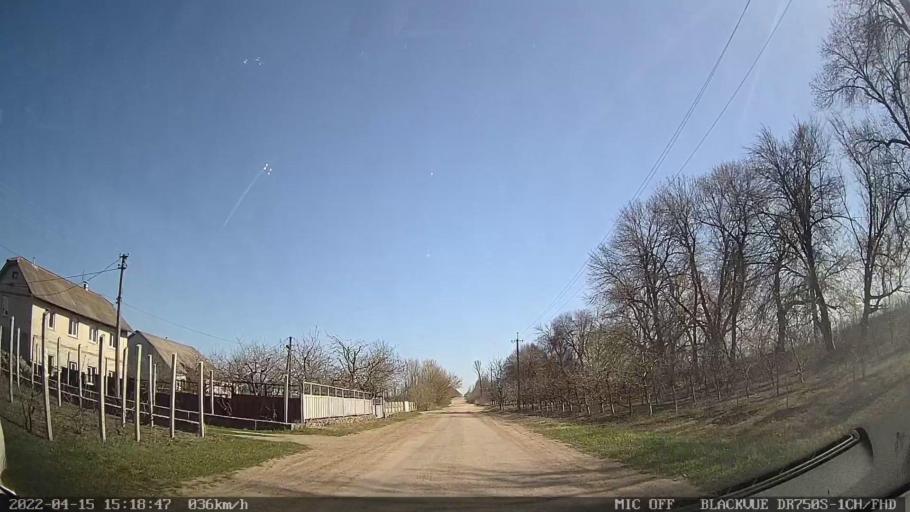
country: MD
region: Raionul Ocnita
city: Otaci
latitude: 48.3893
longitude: 27.9039
